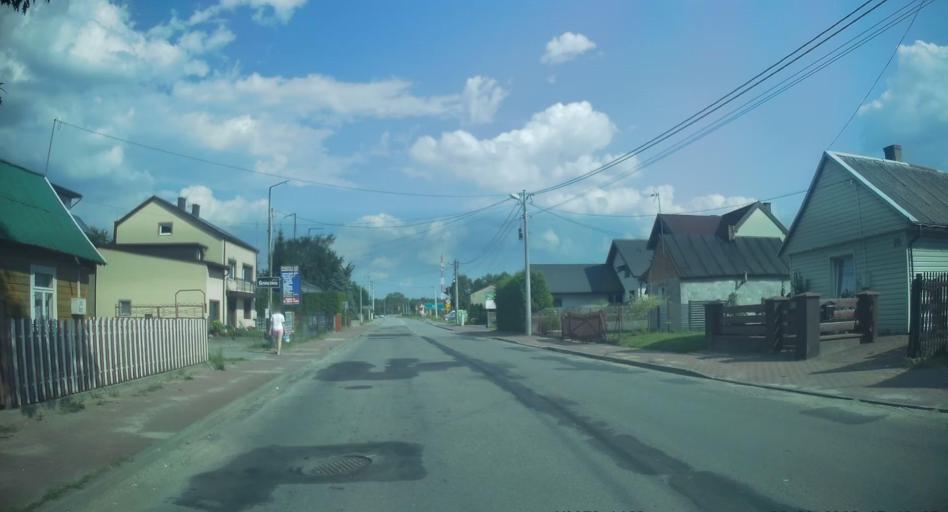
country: PL
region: Swietokrzyskie
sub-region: Powiat konecki
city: Radoszyce
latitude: 51.0724
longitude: 20.2649
